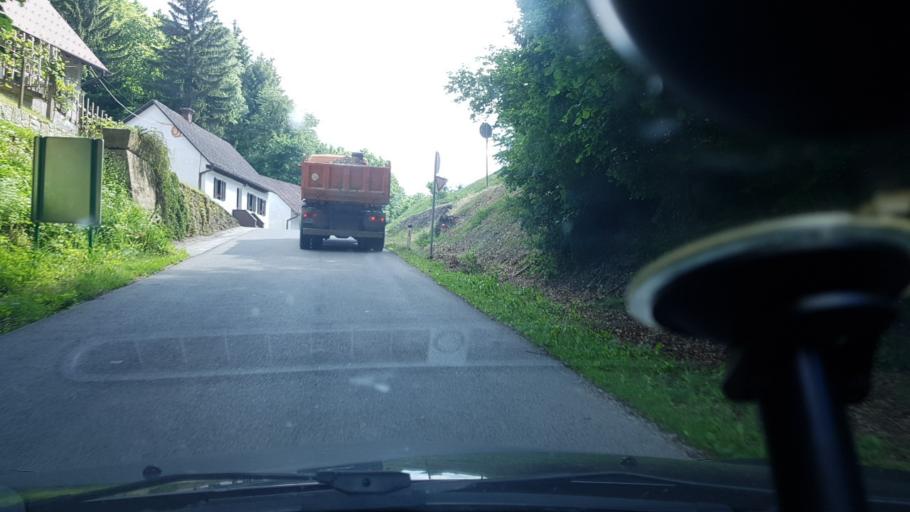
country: SI
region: Rogatec
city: Rogatec
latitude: 46.2591
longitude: 15.7593
